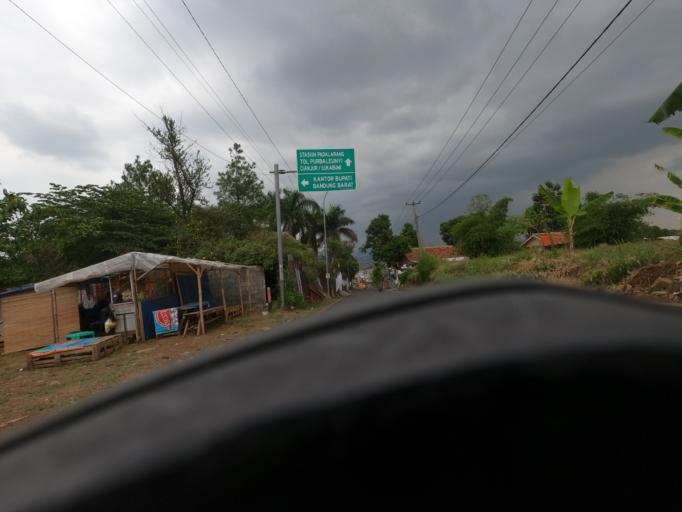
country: ID
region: West Java
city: Padalarang
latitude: -6.8392
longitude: 107.5094
